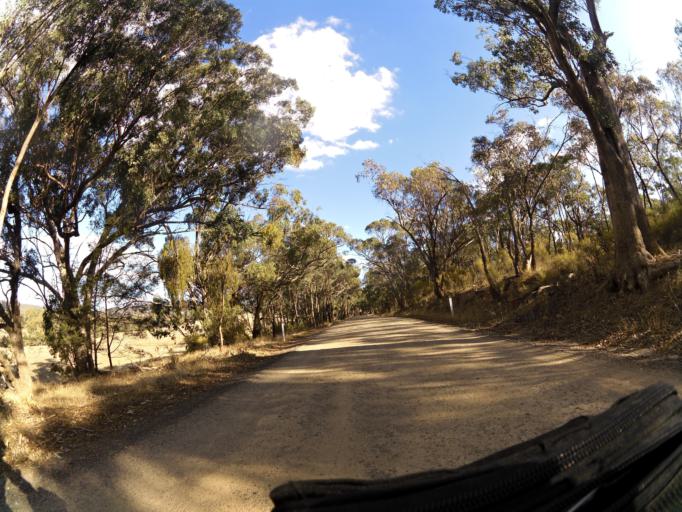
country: AU
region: Victoria
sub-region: Greater Bendigo
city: Kennington
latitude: -37.0151
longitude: 144.8078
